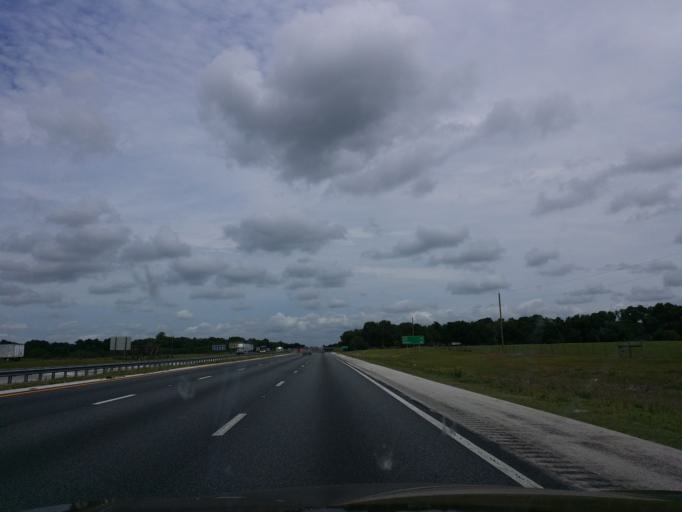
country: US
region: Florida
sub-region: Sumter County
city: Wildwood
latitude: 28.8873
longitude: -82.0962
